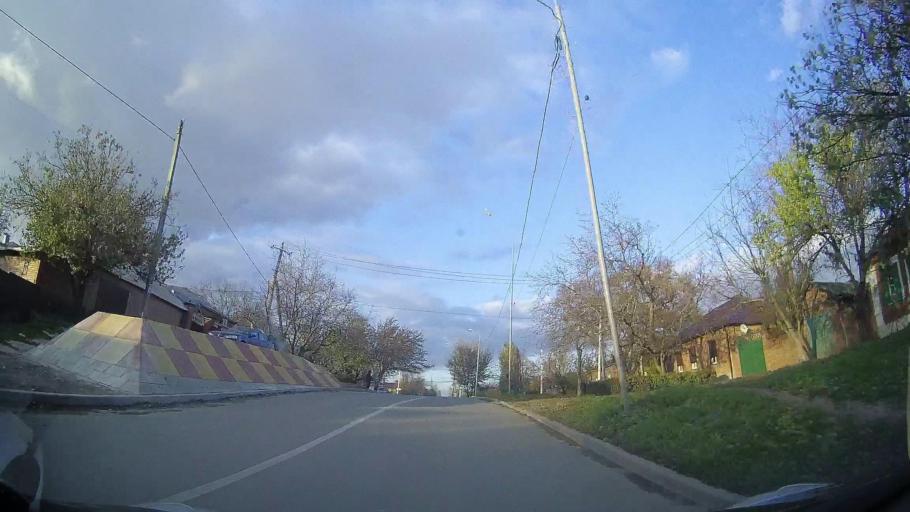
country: RU
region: Rostov
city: Imeni Chkalova
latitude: 47.2431
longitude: 39.7776
